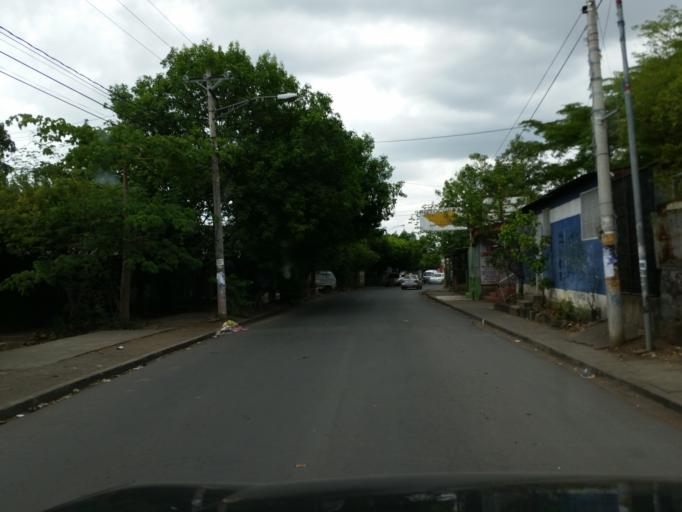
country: NI
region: Managua
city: Managua
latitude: 12.1383
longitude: -86.2241
